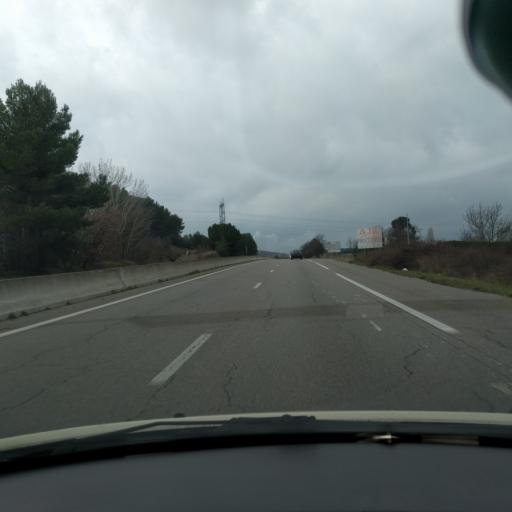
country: FR
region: Provence-Alpes-Cote d'Azur
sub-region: Departement des Bouches-du-Rhone
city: Simiane-Collongue
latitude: 43.4311
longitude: 5.4145
